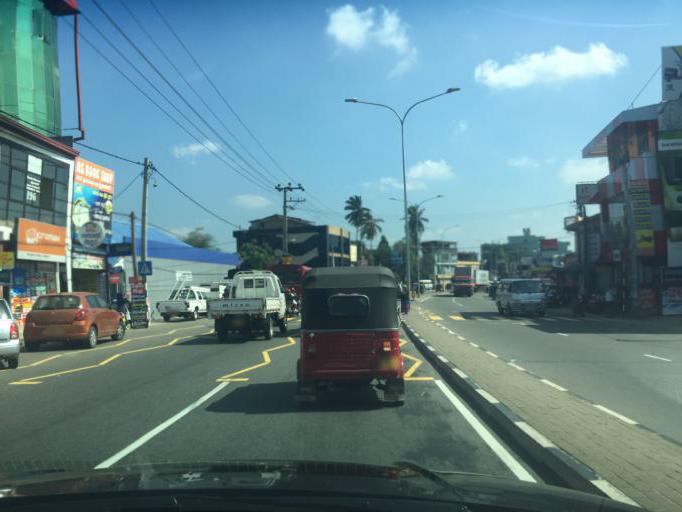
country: LK
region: Western
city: Maharagama
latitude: 6.8399
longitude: 79.9025
